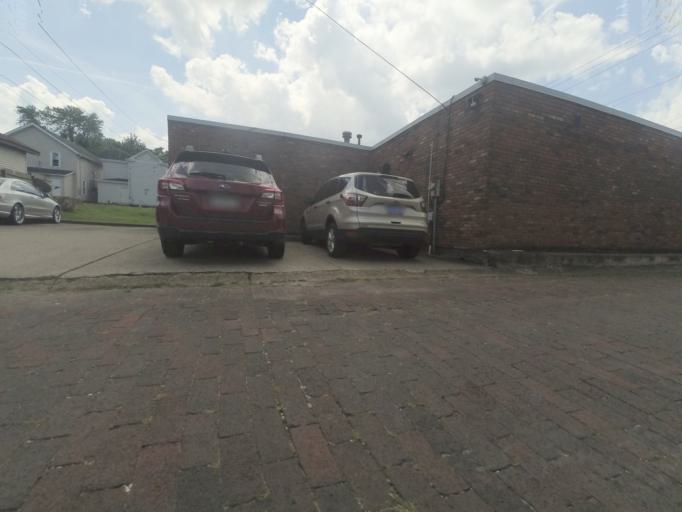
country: US
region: West Virginia
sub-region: Cabell County
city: Huntington
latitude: 38.4155
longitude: -82.4200
